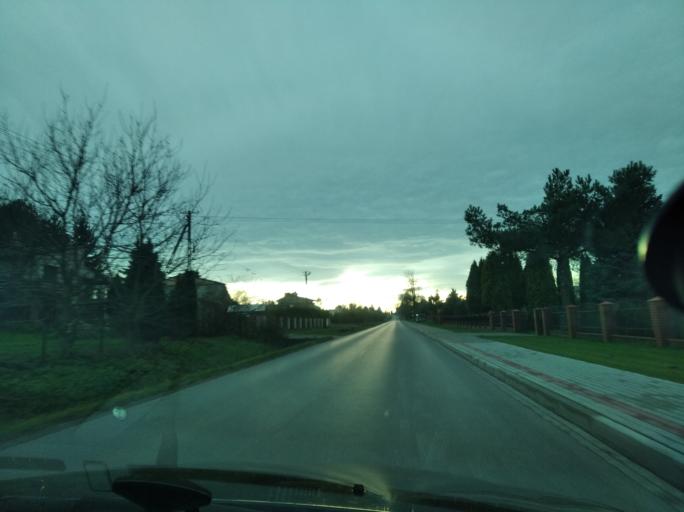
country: PL
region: Subcarpathian Voivodeship
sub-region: Rzeszow
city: Przybyszowka
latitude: 50.0332
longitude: 21.8934
